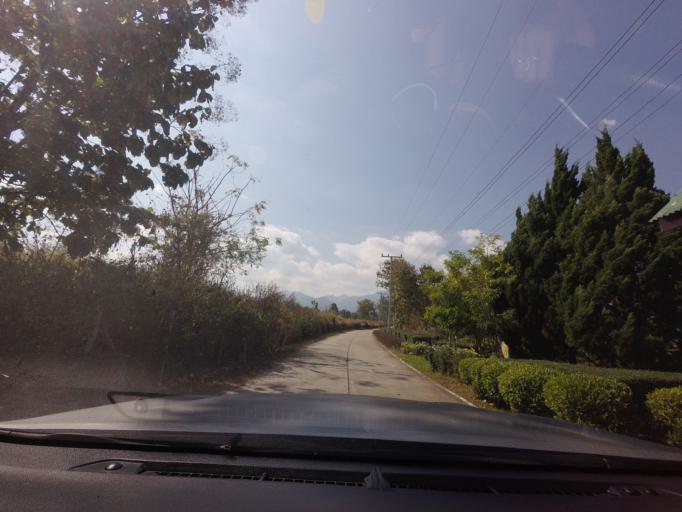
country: TH
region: Mae Hong Son
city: Wiang Nuea
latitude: 19.3832
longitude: 98.4309
